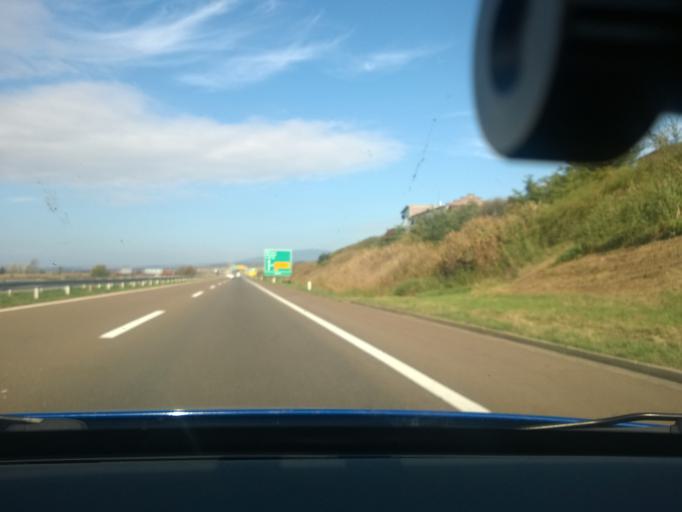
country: RS
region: Central Serbia
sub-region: Nisavski Okrug
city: Aleksinac
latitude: 43.5428
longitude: 21.6910
